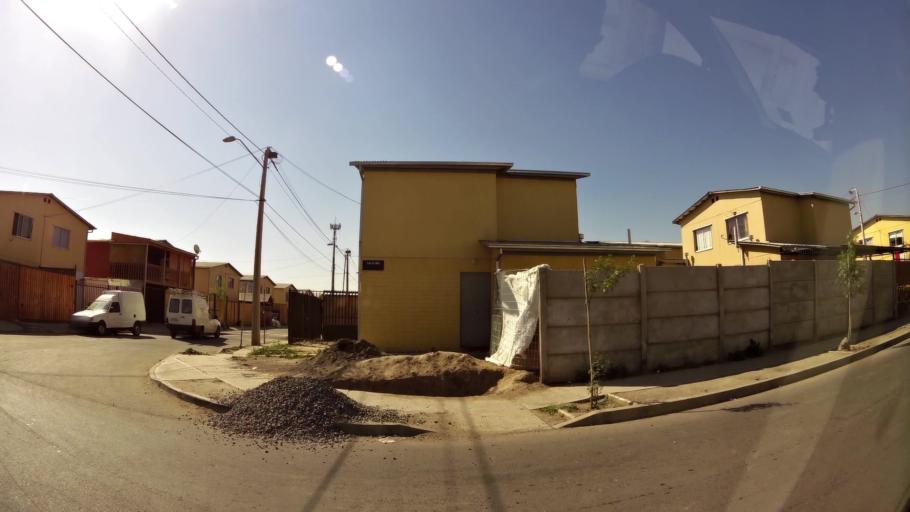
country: CL
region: Santiago Metropolitan
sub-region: Provincia de Santiago
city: La Pintana
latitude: -33.6199
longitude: -70.6218
